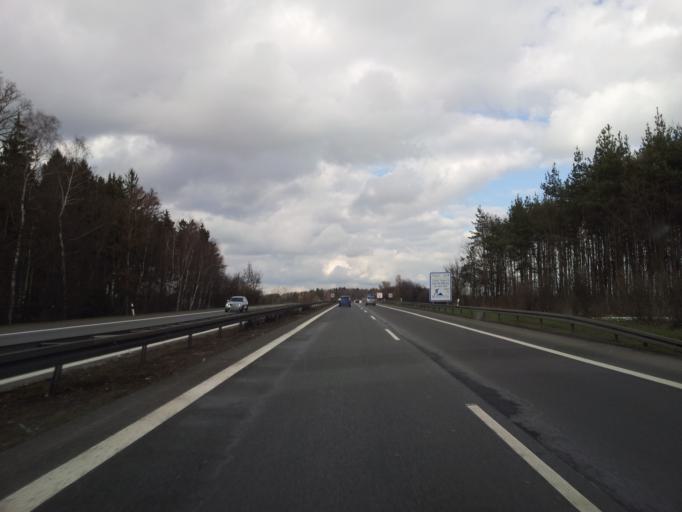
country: DE
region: Saxony
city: Waldkirchen
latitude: 50.6017
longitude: 12.3663
